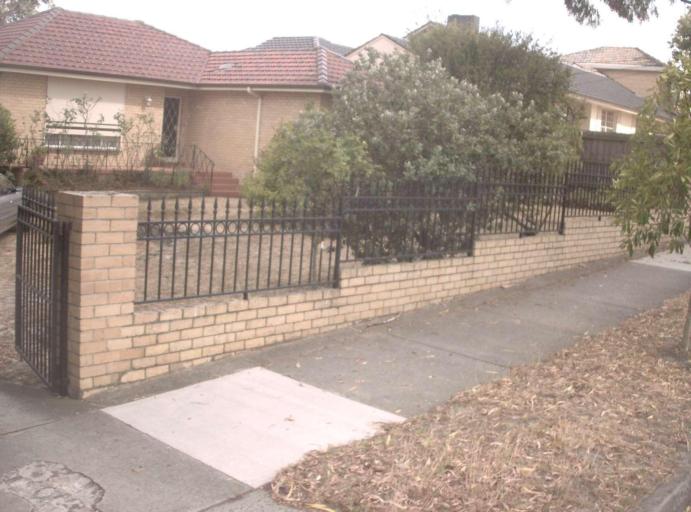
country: AU
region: Victoria
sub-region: Monash
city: Ashwood
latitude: -37.8648
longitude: 145.1123
